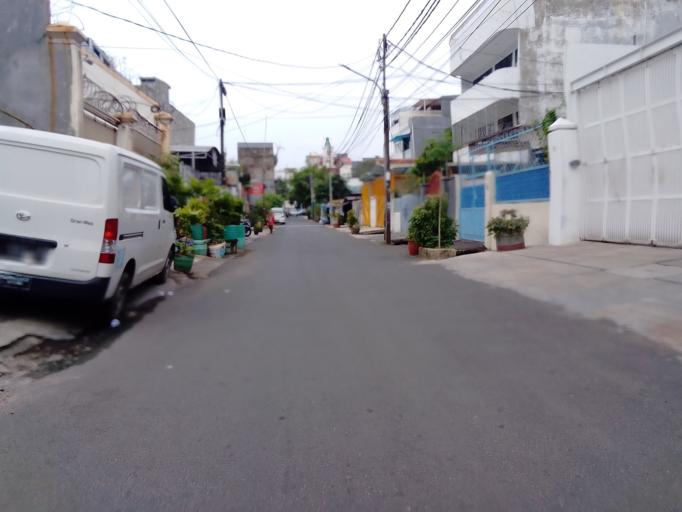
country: ID
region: Jakarta Raya
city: Jakarta
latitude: -6.1563
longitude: 106.8169
